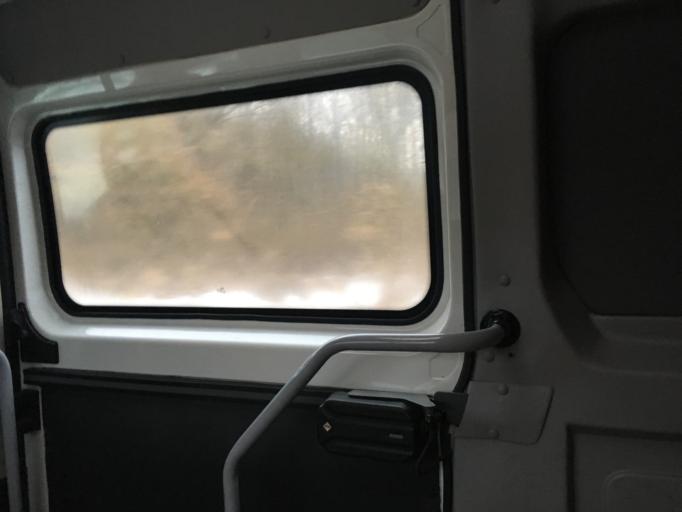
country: RU
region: Tula
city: Dubna
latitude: 54.1032
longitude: 37.1083
